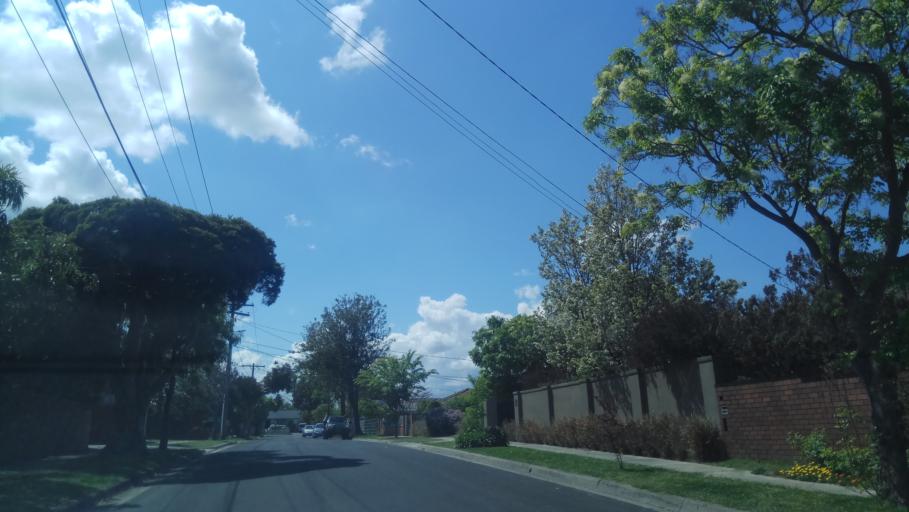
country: AU
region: Victoria
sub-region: Kingston
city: Dingley Village
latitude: -37.9846
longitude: 145.1380
